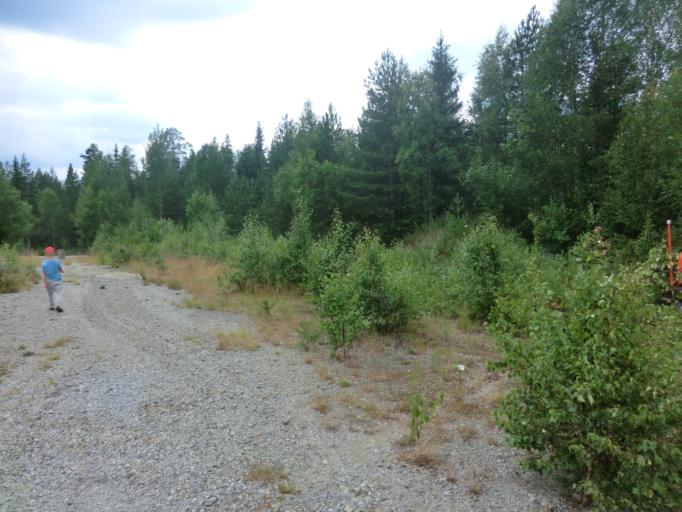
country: SE
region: Vaesterbotten
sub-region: Lycksele Kommun
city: Lycksele
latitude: 64.0806
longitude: 18.3485
